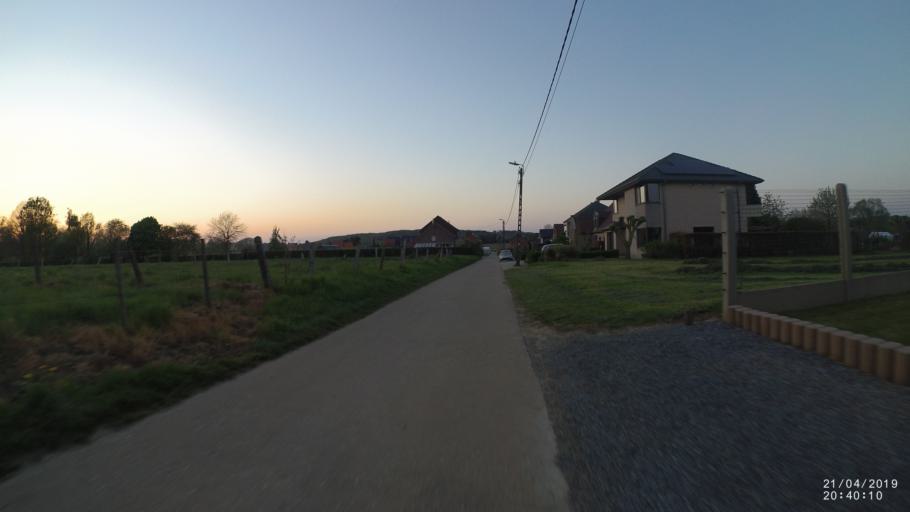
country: BE
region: Flanders
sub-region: Provincie Vlaams-Brabant
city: Lubbeek
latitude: 50.9019
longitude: 4.8586
